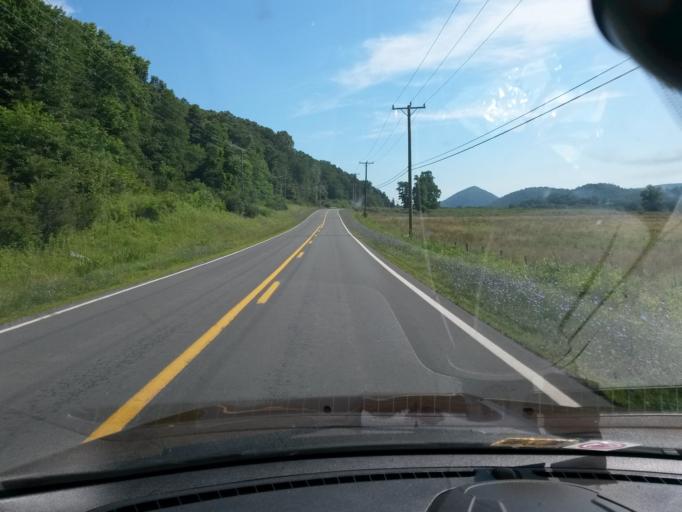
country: US
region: West Virginia
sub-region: Hardy County
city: Moorefield
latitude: 39.0320
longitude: -78.7530
